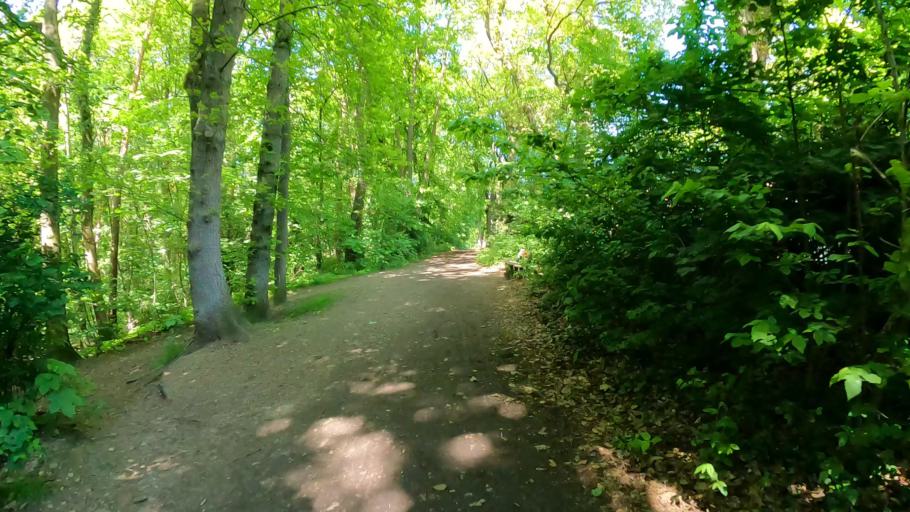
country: DE
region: Hamburg
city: Harburg
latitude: 53.4639
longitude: 9.9445
